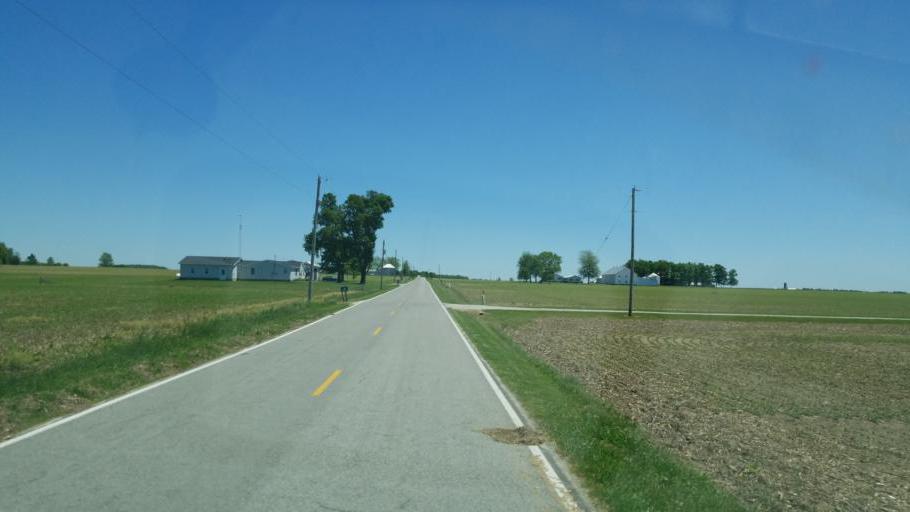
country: US
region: Ohio
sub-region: Darke County
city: Union City
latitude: 40.2813
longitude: -84.7357
